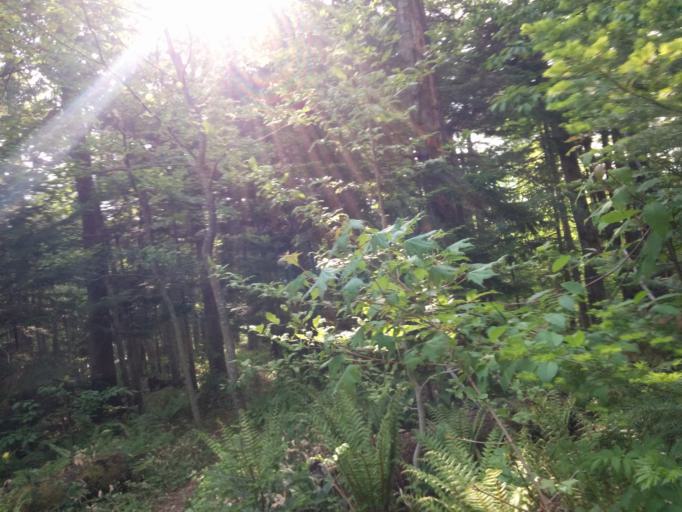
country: JP
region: Hokkaido
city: Bihoro
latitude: 43.4346
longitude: 144.1032
